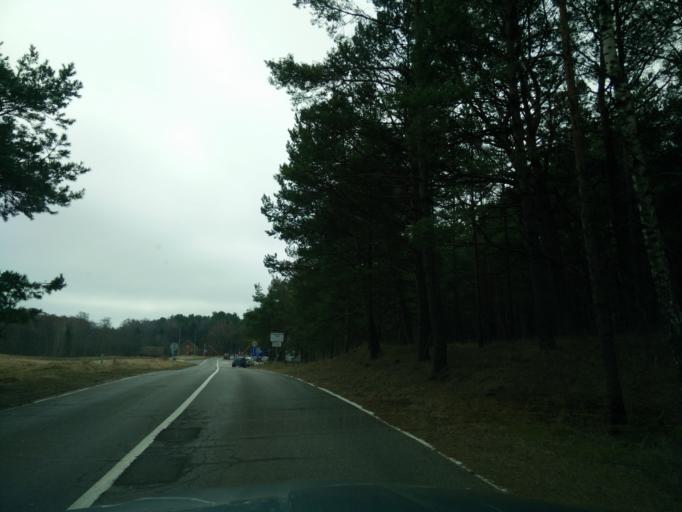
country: LT
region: Klaipedos apskritis
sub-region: Klaipeda
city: Klaipeda
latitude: 55.6346
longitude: 21.1299
